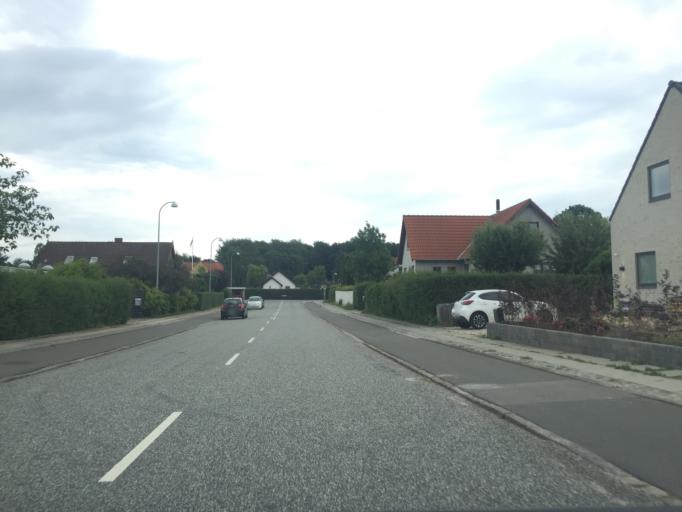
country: DK
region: Capital Region
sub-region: Lyngby-Tarbaek Kommune
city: Kongens Lyngby
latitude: 55.7948
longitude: 12.5399
